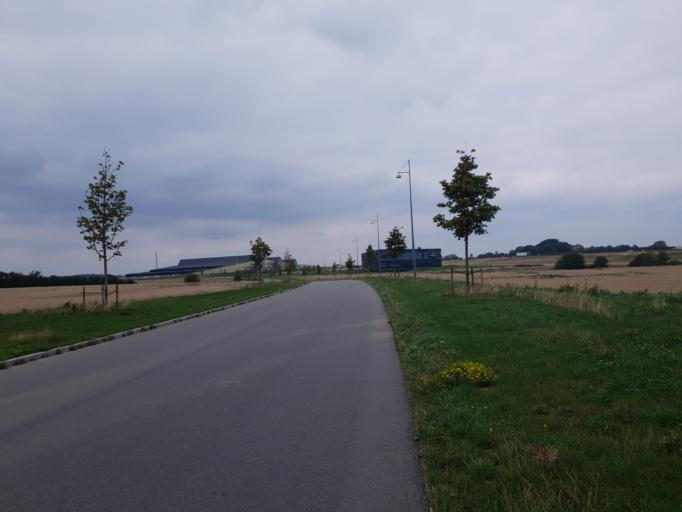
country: DK
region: South Denmark
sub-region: Middelfart Kommune
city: Strib
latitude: 55.4976
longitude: 9.7880
